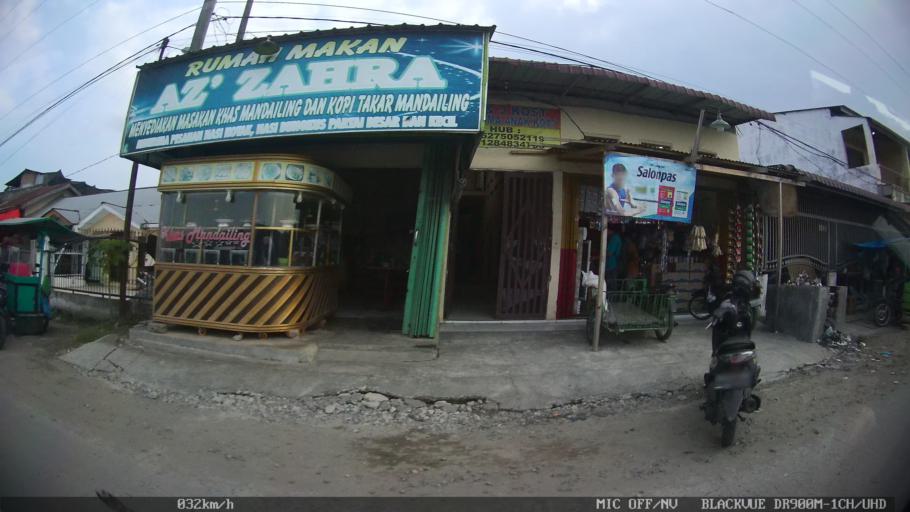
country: ID
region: North Sumatra
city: Medan
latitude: 3.6057
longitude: 98.7282
